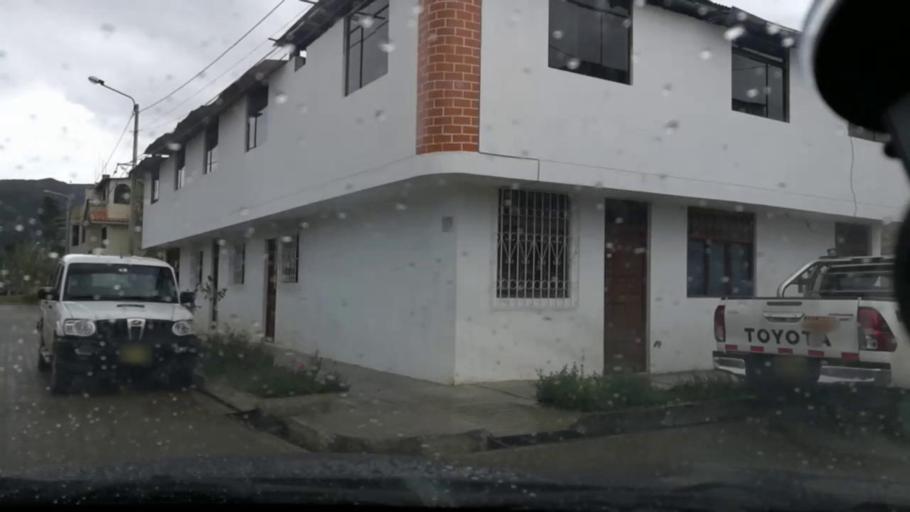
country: PE
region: Cajamarca
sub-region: Provincia de Cajamarca
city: Cajamarca
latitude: -7.1609
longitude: -78.4697
